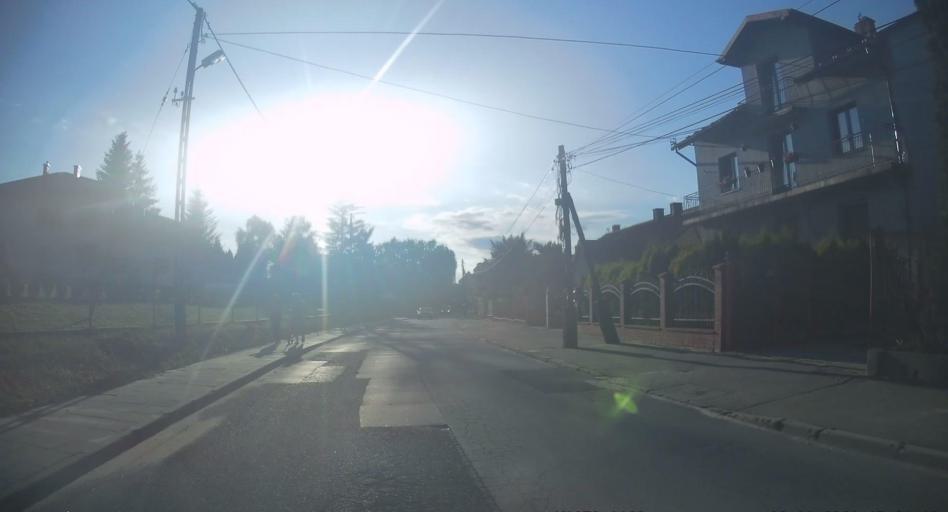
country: PL
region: Lesser Poland Voivodeship
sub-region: Powiat wielicki
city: Czarnochowice
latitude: 50.0173
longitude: 20.0460
